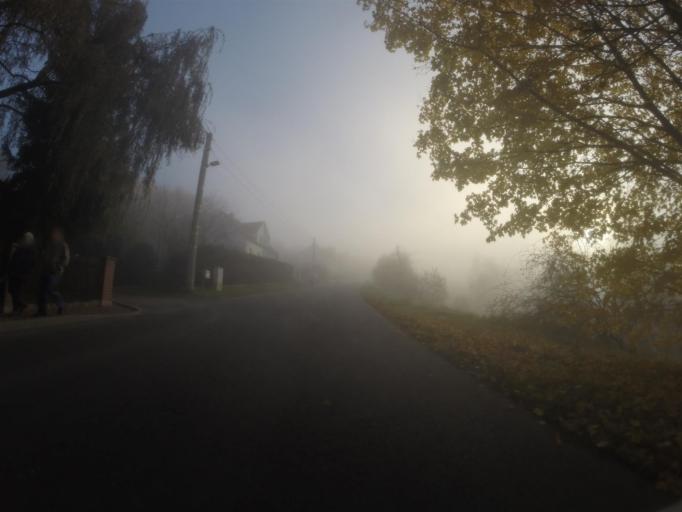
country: DE
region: Thuringia
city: Eisenberg
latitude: 50.9738
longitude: 11.9055
